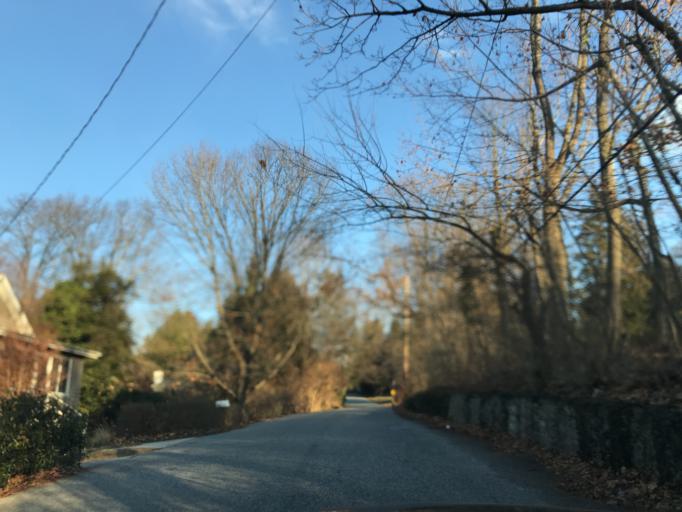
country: US
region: Maryland
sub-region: Baltimore County
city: Lutherville
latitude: 39.3976
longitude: -76.6443
